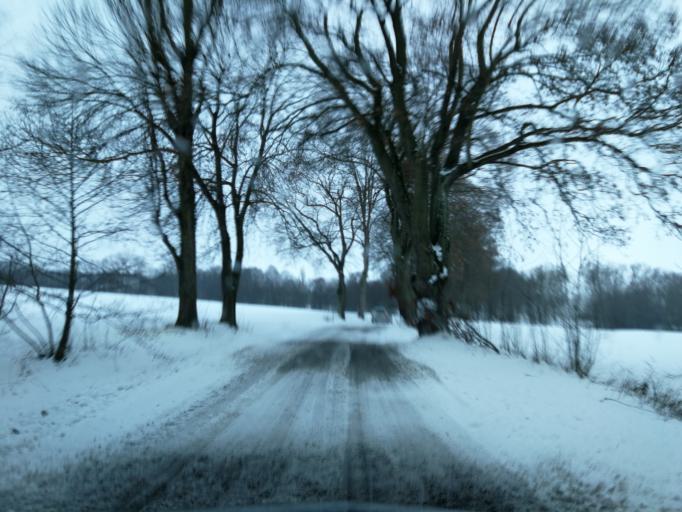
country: CZ
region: Vysocina
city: Heralec
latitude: 49.5332
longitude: 15.4448
